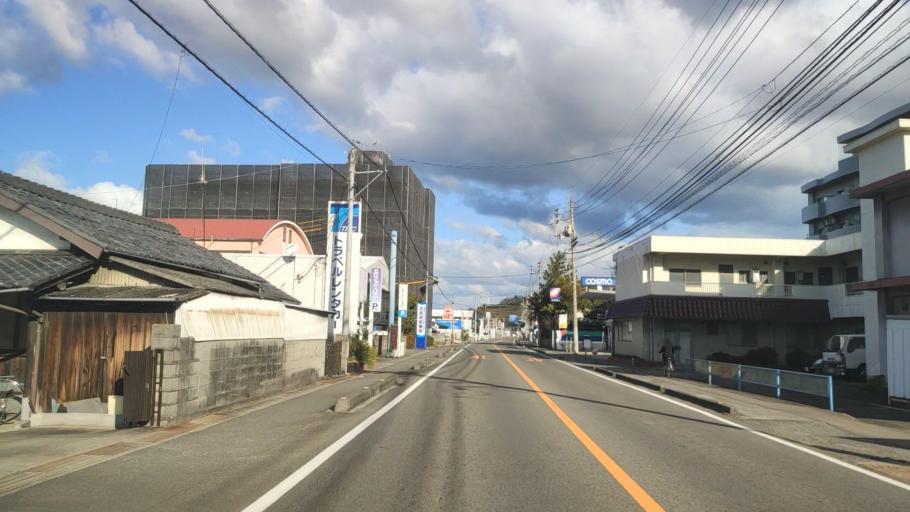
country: JP
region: Ehime
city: Masaki-cho
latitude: 33.8332
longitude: 132.7093
